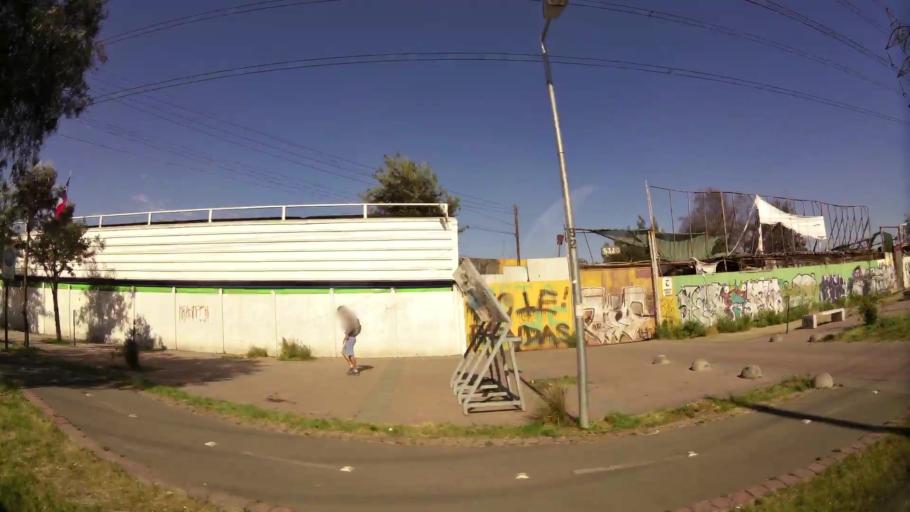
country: CL
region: Santiago Metropolitan
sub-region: Provincia de Santiago
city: Santiago
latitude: -33.4965
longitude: -70.6776
